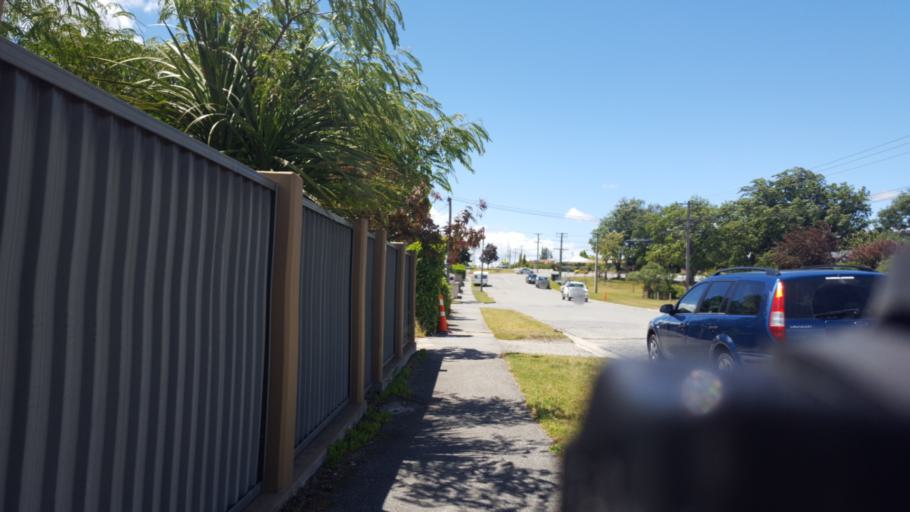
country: NZ
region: Otago
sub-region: Queenstown-Lakes District
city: Wanaka
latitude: -45.2510
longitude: 169.3944
